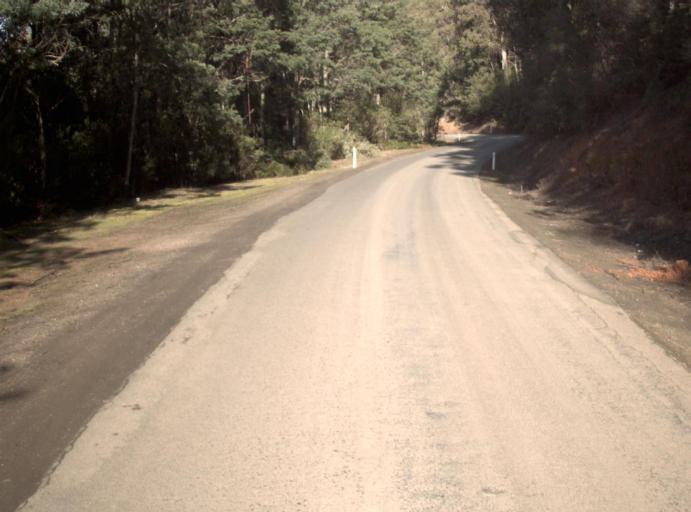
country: AU
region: Tasmania
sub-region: Dorset
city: Scottsdale
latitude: -41.3165
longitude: 147.4049
